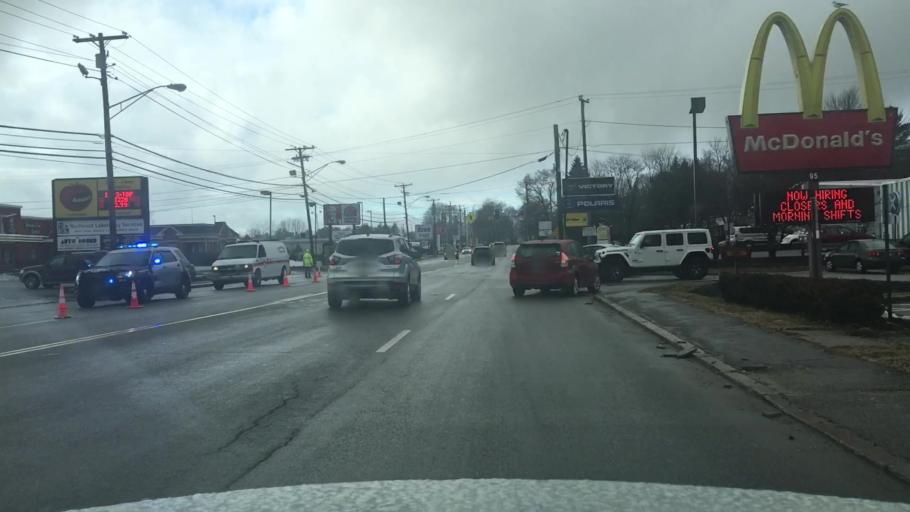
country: US
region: Maine
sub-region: Cumberland County
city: Westbrook
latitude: 43.6780
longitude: -70.3349
